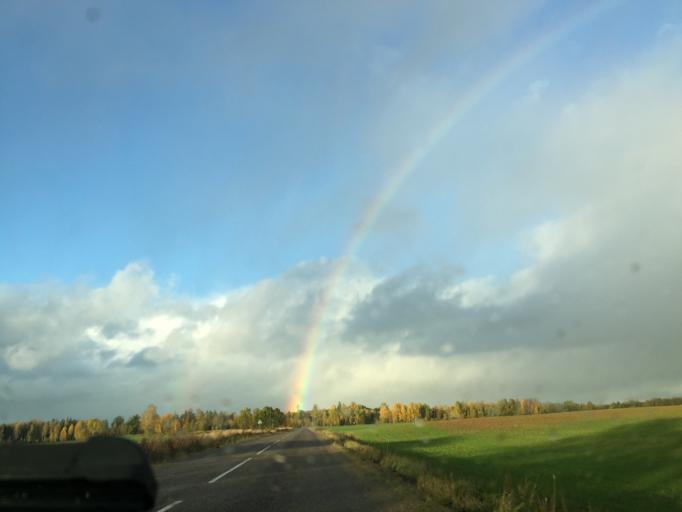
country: LV
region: Broceni
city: Broceni
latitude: 56.8792
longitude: 22.3818
